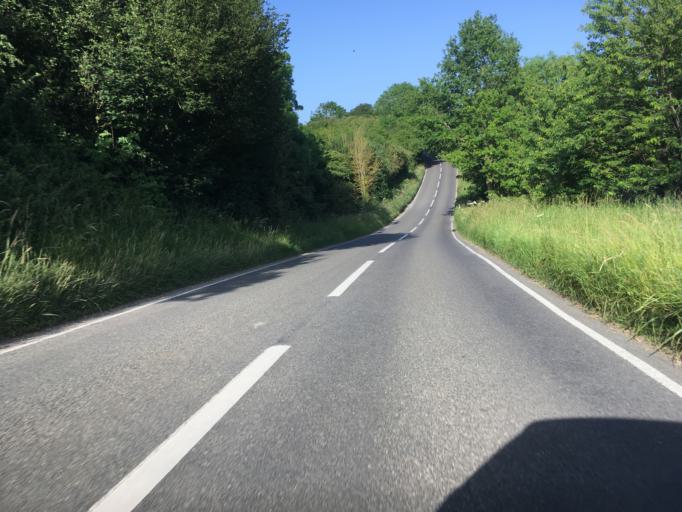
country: GB
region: England
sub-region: Oxfordshire
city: Shipton under Wychwood
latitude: 51.8555
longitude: -1.5679
